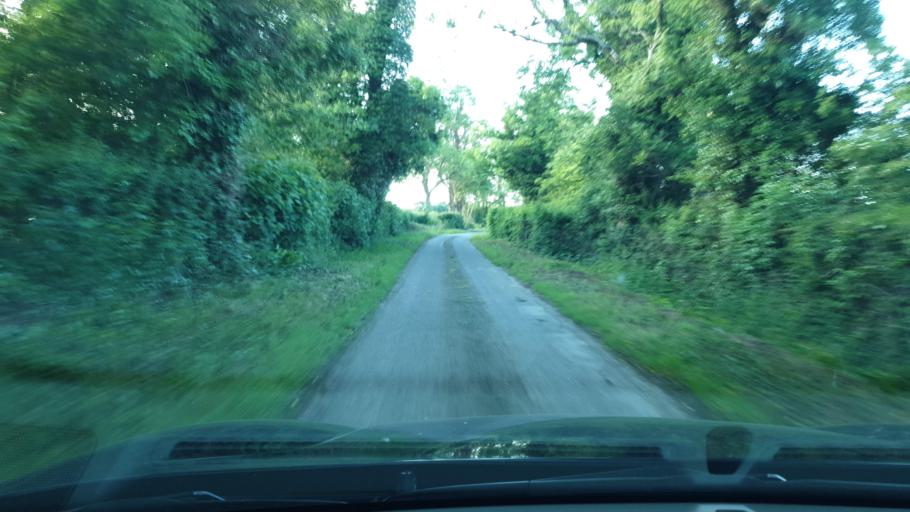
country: IE
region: Leinster
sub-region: An Mhi
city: Ashbourne
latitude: 53.4551
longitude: -6.4086
